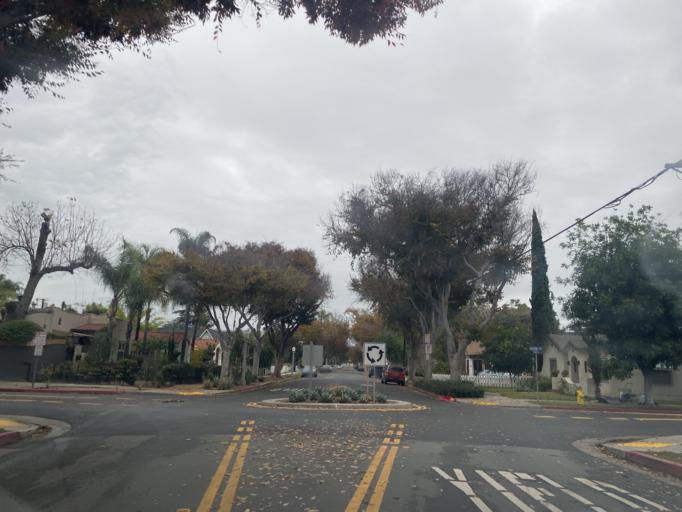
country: US
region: California
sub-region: Orange County
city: Fullerton
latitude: 33.8724
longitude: -117.9157
